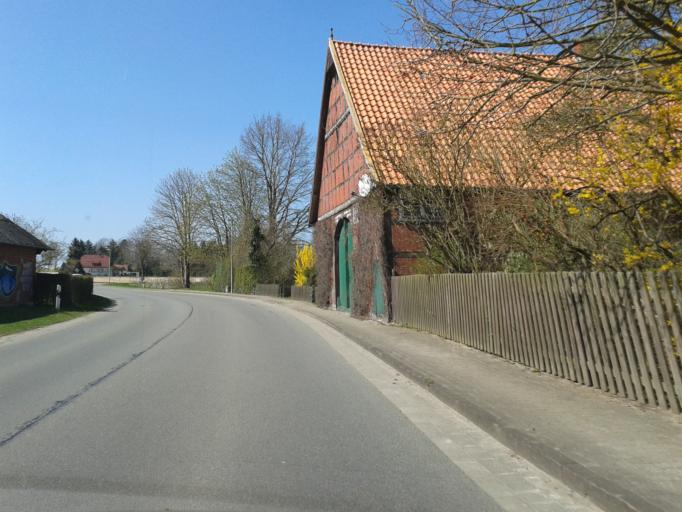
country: DE
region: Lower Saxony
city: Kusten
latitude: 52.9419
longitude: 11.0715
